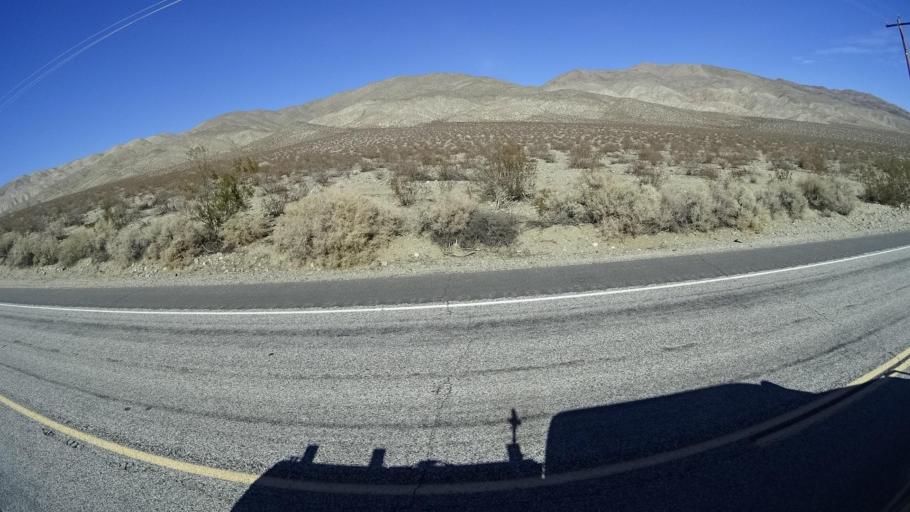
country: US
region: California
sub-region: Kern County
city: Inyokern
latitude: 35.3766
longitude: -117.8616
